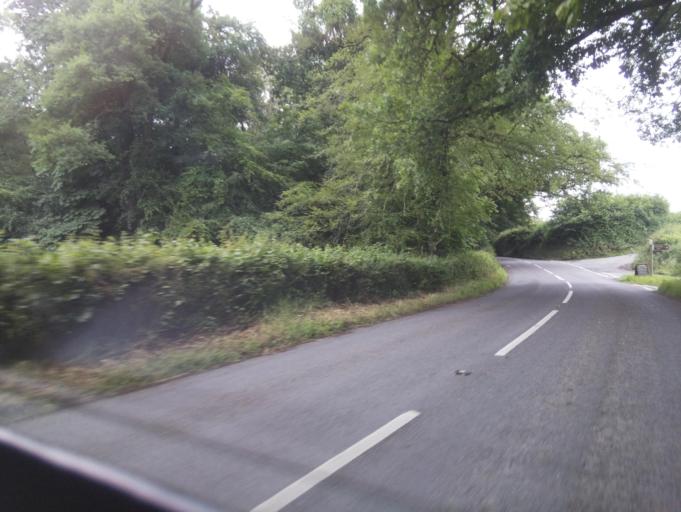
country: GB
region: England
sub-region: Devon
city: Chudleigh
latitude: 50.6288
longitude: -3.6413
